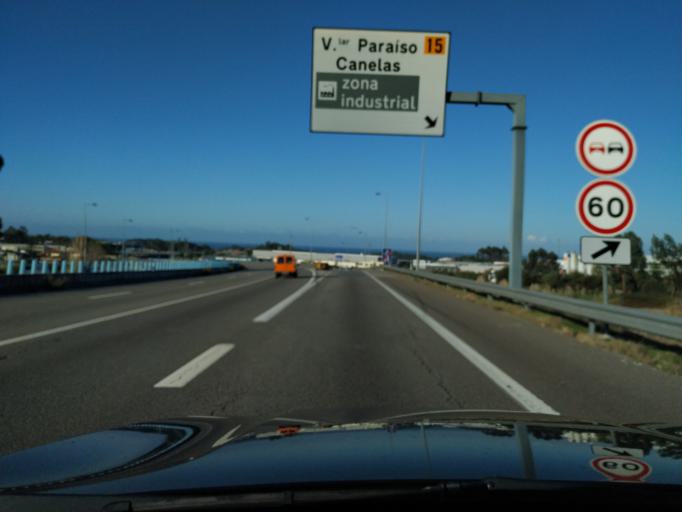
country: PT
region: Porto
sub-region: Vila Nova de Gaia
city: Canelas
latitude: 41.0899
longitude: -8.5996
